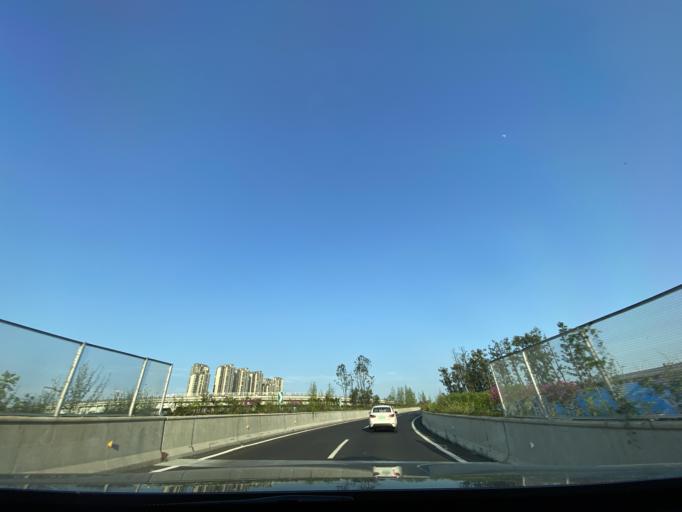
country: CN
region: Sichuan
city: Chengdu
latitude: 30.5988
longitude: 104.1152
